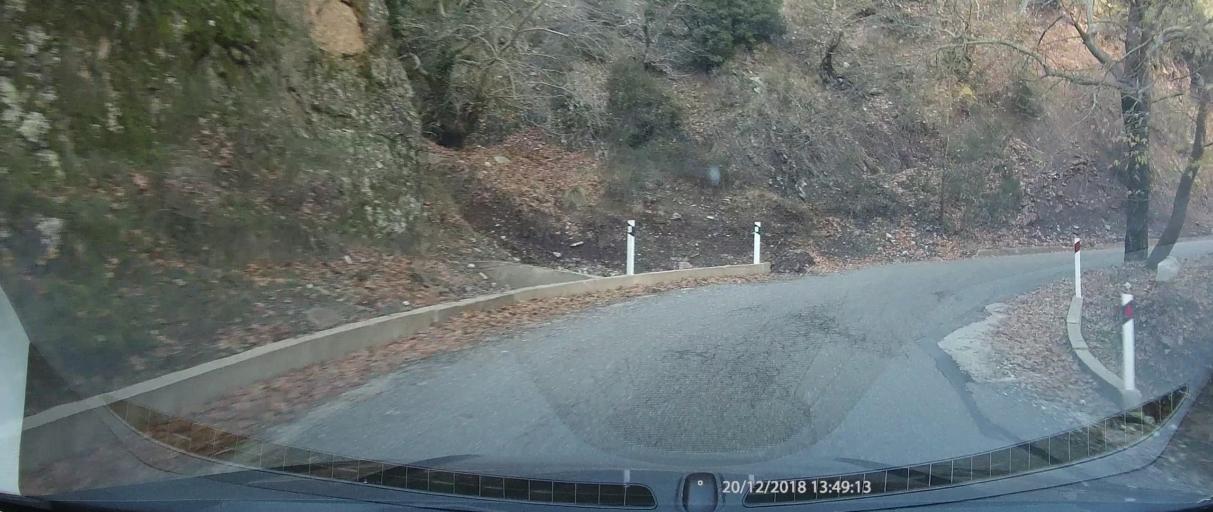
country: GR
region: West Greece
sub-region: Nomos Aitolias kai Akarnanias
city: Paravola
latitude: 38.6912
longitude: 21.6071
